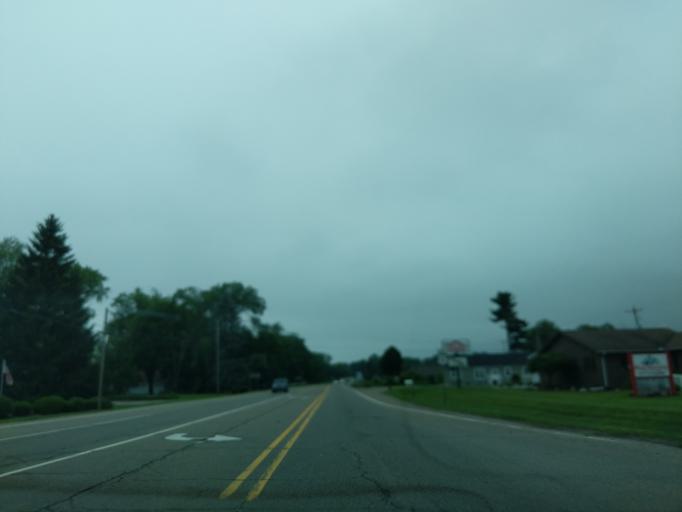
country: US
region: Michigan
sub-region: Branch County
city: Quincy
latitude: 41.9398
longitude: -84.9319
